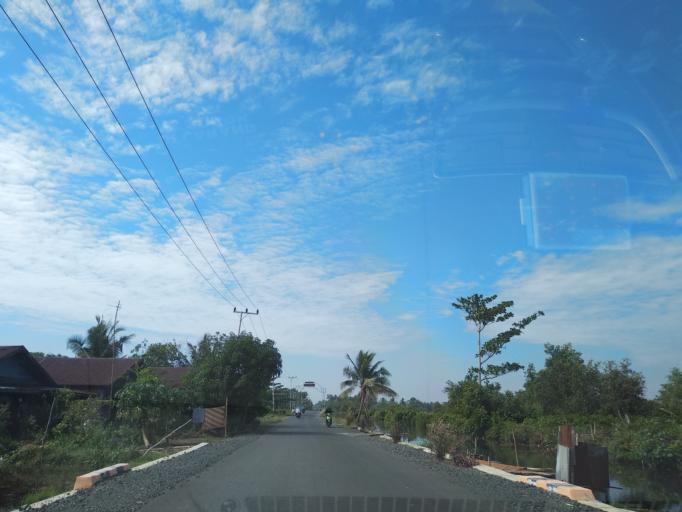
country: ID
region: South Kalimantan
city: Banjarmasin
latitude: -3.3004
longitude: 114.4830
